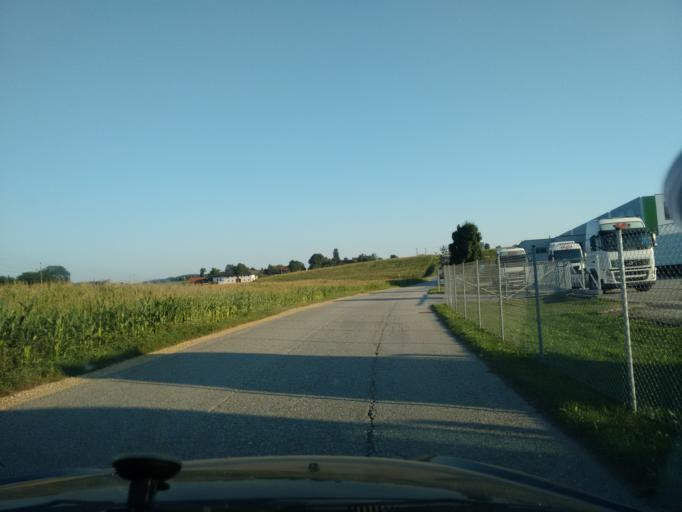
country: AT
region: Upper Austria
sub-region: Politischer Bezirk Grieskirchen
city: Bad Schallerbach
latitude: 48.2190
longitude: 13.9468
